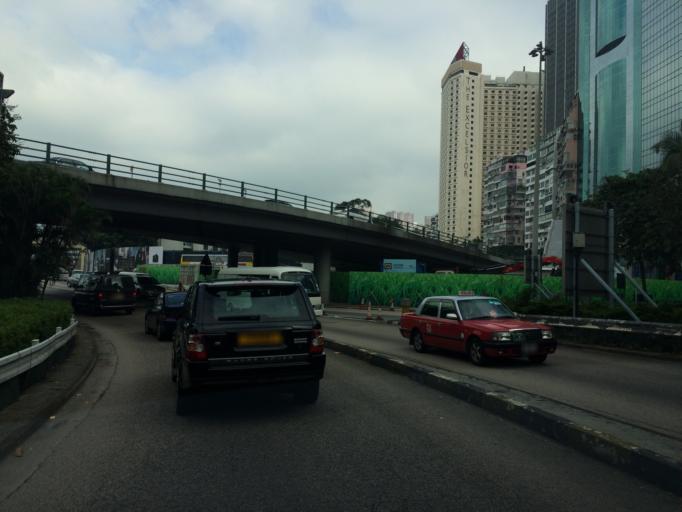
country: HK
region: Wanchai
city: Wan Chai
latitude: 22.2819
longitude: 114.1812
